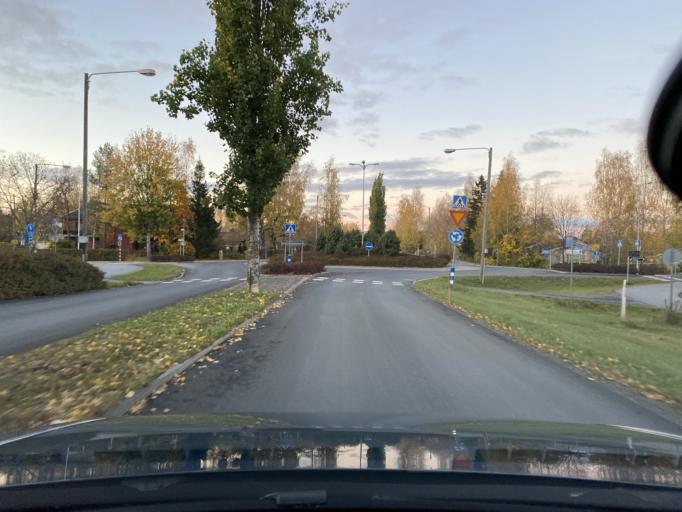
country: FI
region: Pirkanmaa
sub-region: Tampere
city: Lempaeaelae
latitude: 61.3252
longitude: 23.7485
